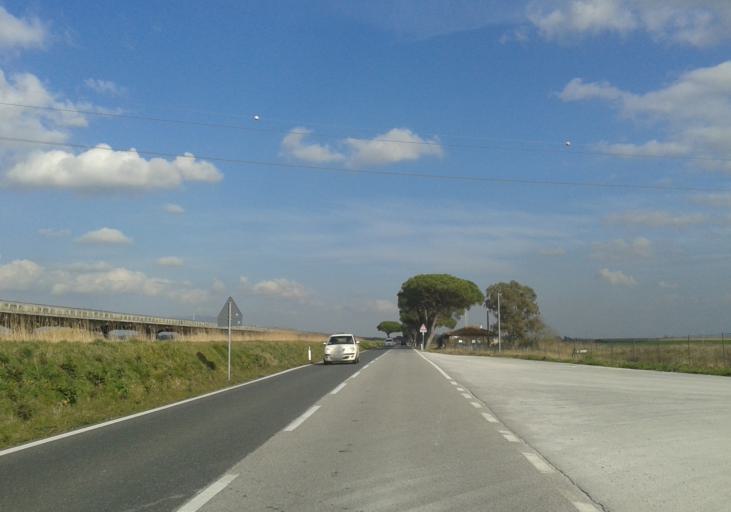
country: IT
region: Tuscany
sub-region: Provincia di Livorno
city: Guasticce
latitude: 43.6109
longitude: 10.3831
